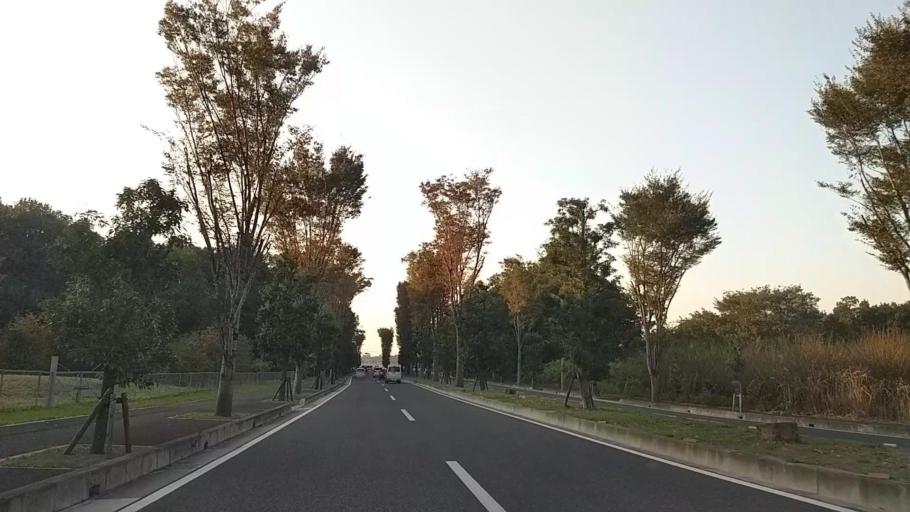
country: JP
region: Saitama
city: Sayama
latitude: 35.8429
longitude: 139.4537
